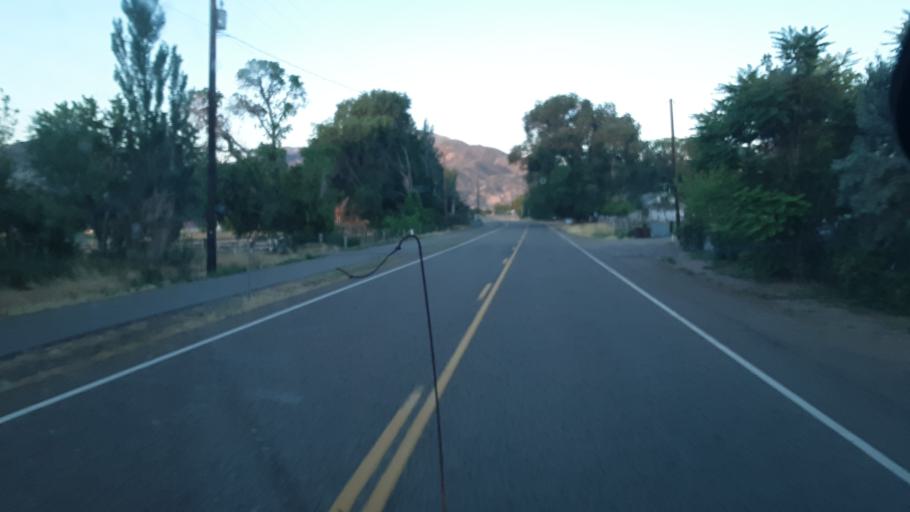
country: US
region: Utah
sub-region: Sevier County
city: Monroe
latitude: 38.5983
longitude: -112.2463
